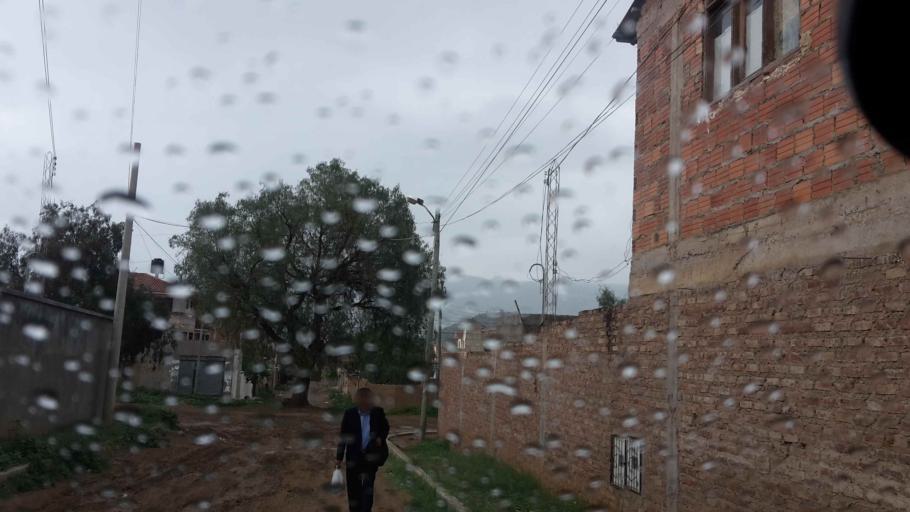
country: BO
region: Cochabamba
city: Cochabamba
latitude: -17.4474
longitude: -66.1567
